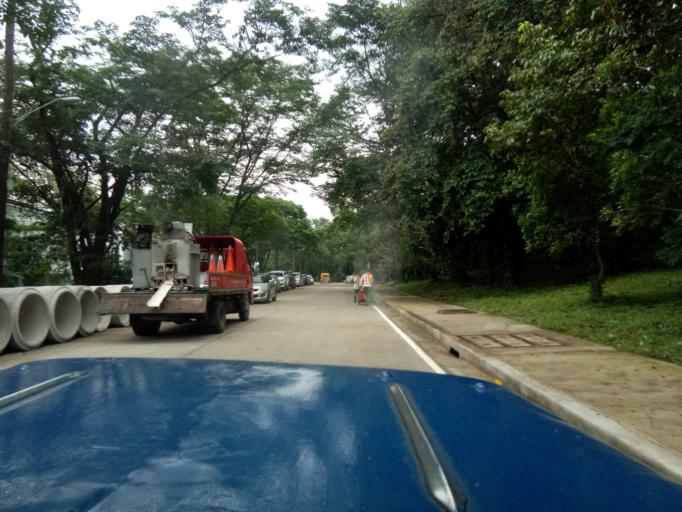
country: PH
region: Metro Manila
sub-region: Quezon City
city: Quezon City
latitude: 14.6508
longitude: 121.0662
